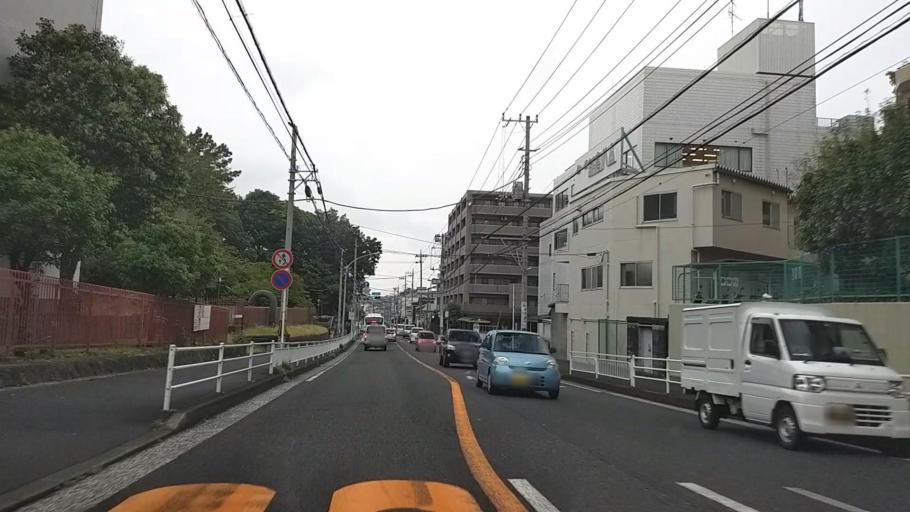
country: JP
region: Kanagawa
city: Yokohama
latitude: 35.4080
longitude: 139.6117
